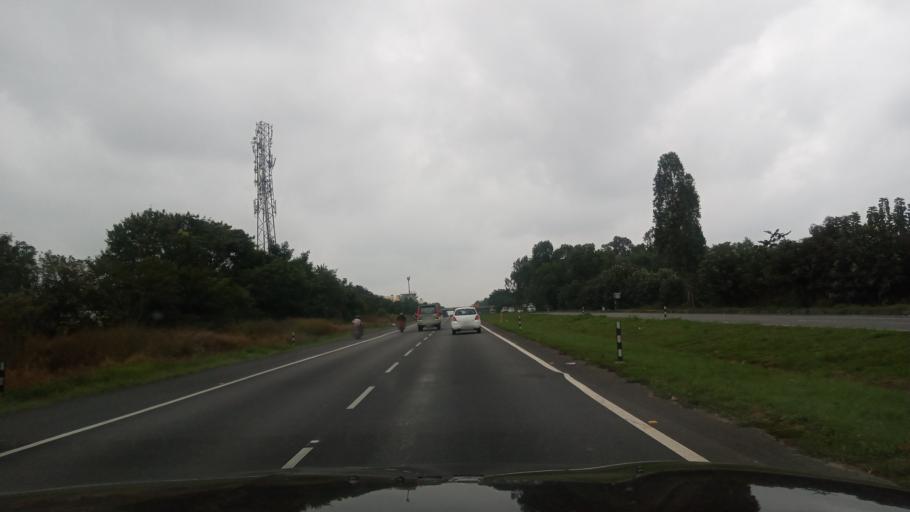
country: IN
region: Karnataka
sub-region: Bangalore Urban
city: Bangalore
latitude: 12.8646
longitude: 77.6442
